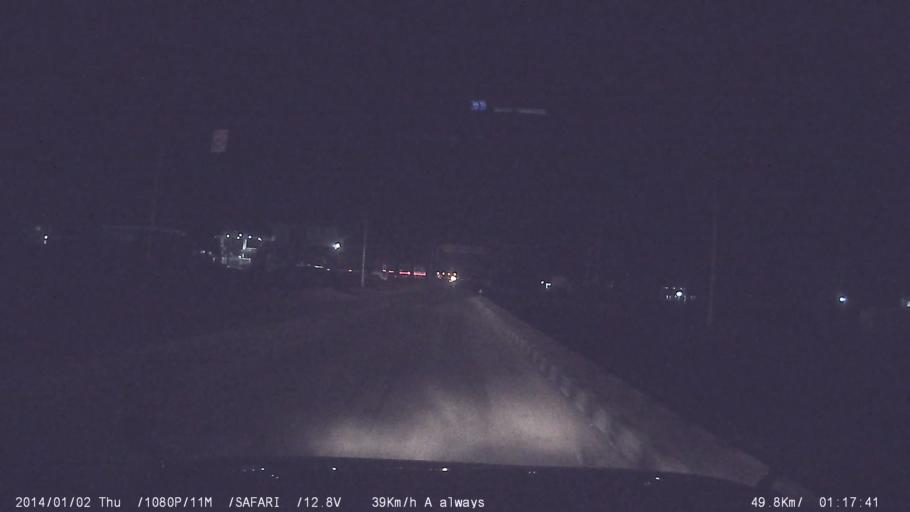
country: IN
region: Tamil Nadu
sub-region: Coimbatore
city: Irugur
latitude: 11.0077
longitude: 77.0706
